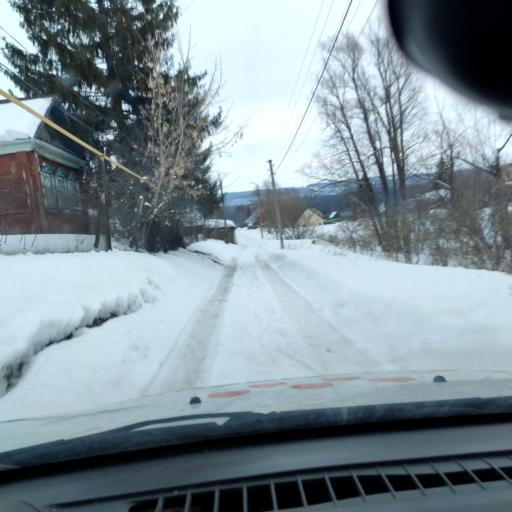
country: RU
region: Bashkortostan
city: Avdon
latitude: 54.6197
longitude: 55.6492
